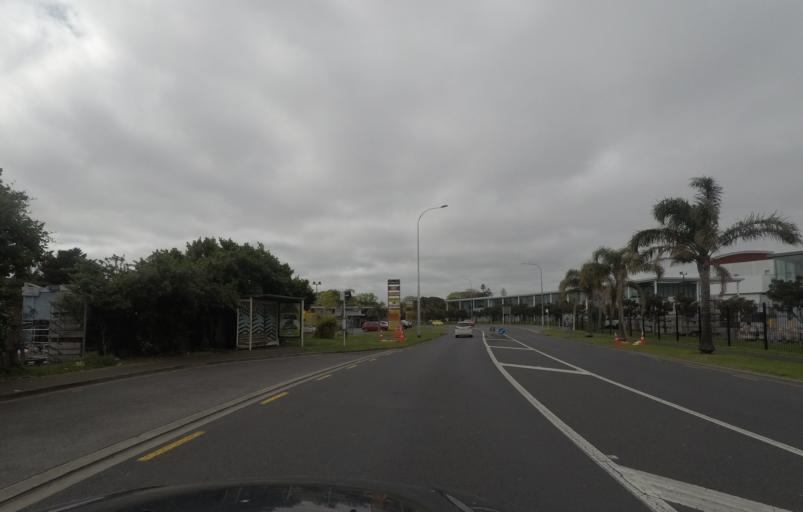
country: NZ
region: Auckland
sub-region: Auckland
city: Wiri
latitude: -36.9574
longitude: 174.8539
